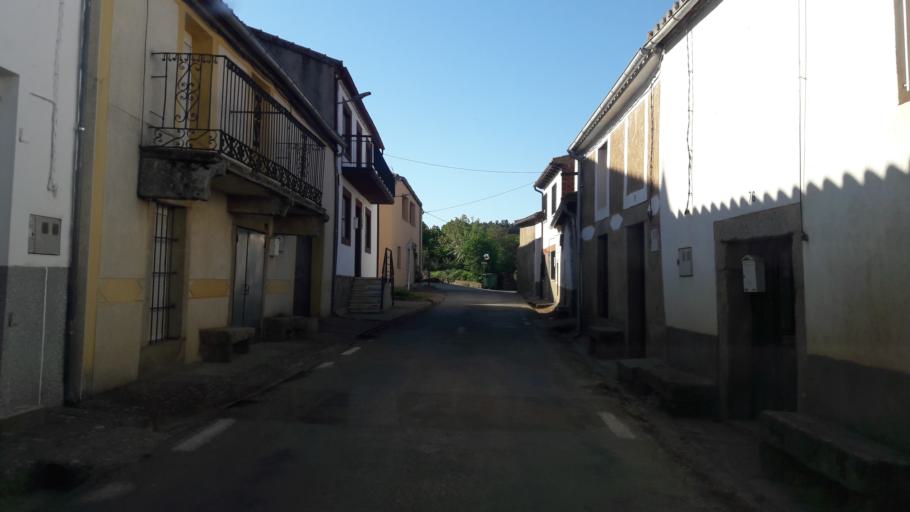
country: ES
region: Castille and Leon
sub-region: Provincia de Salamanca
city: Endrinal
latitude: 40.5893
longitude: -5.8036
